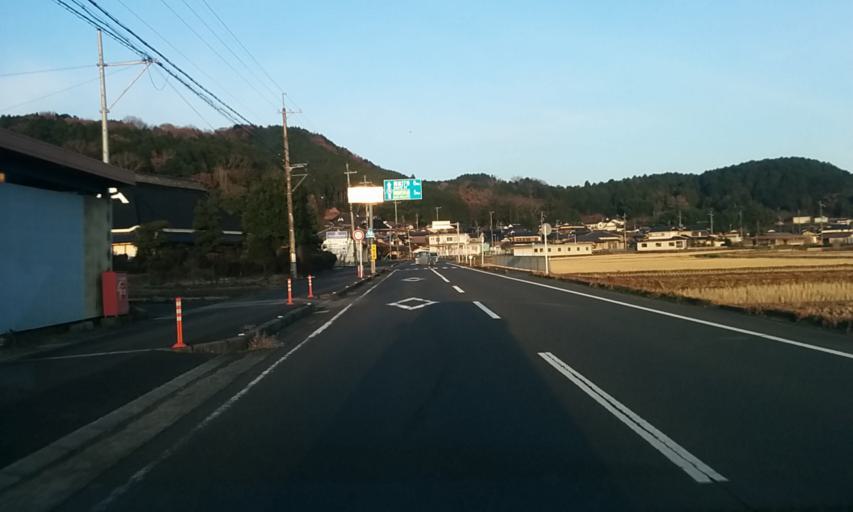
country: JP
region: Kyoto
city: Ayabe
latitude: 35.3139
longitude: 135.2234
